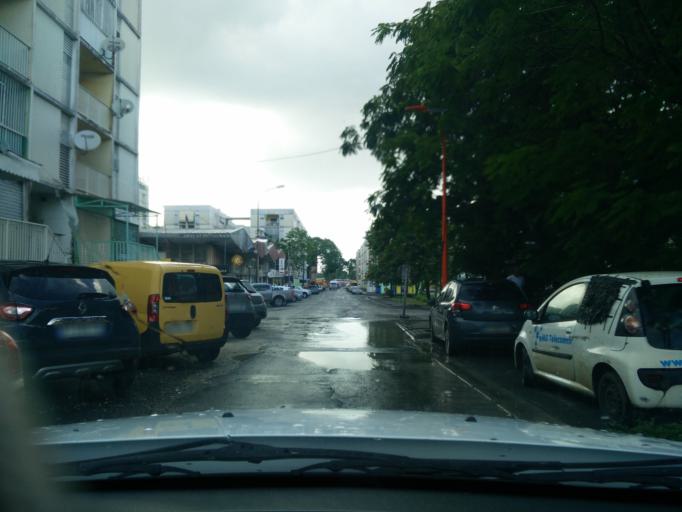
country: GP
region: Guadeloupe
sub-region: Guadeloupe
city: Pointe-a-Pitre
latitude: 16.2519
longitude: -61.5383
